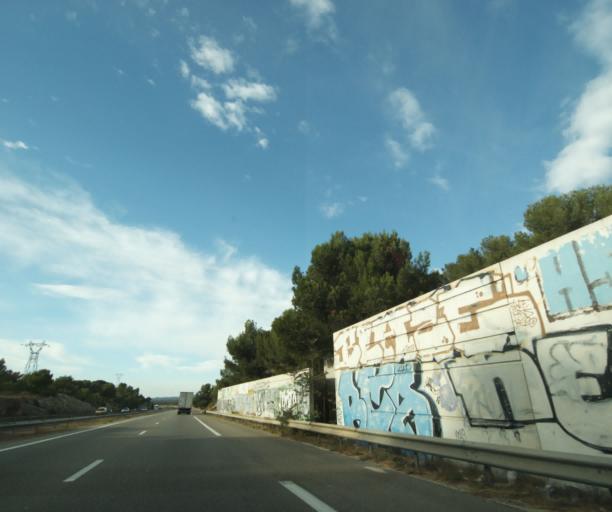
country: FR
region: Provence-Alpes-Cote d'Azur
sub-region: Departement des Bouches-du-Rhone
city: Chateauneuf-les-Martigues
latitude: 43.3836
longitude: 5.1532
